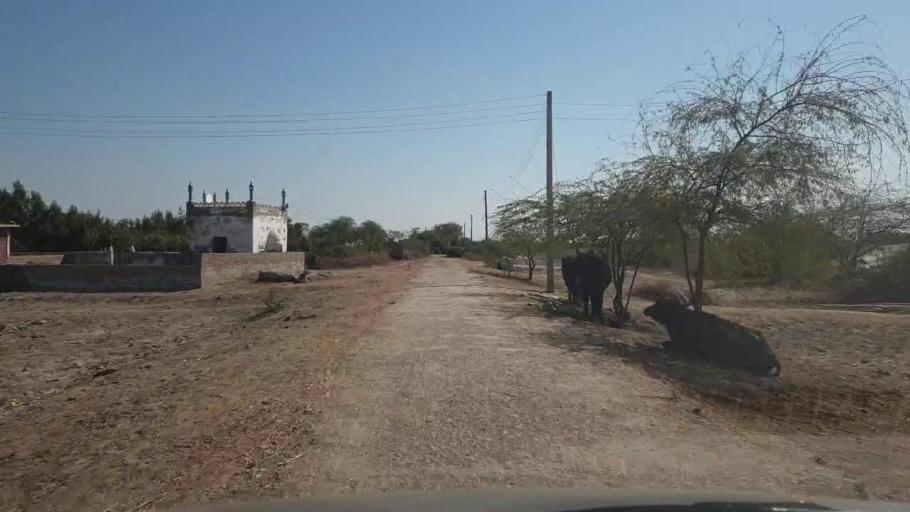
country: PK
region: Sindh
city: Dhoro Naro
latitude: 25.4001
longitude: 69.6124
